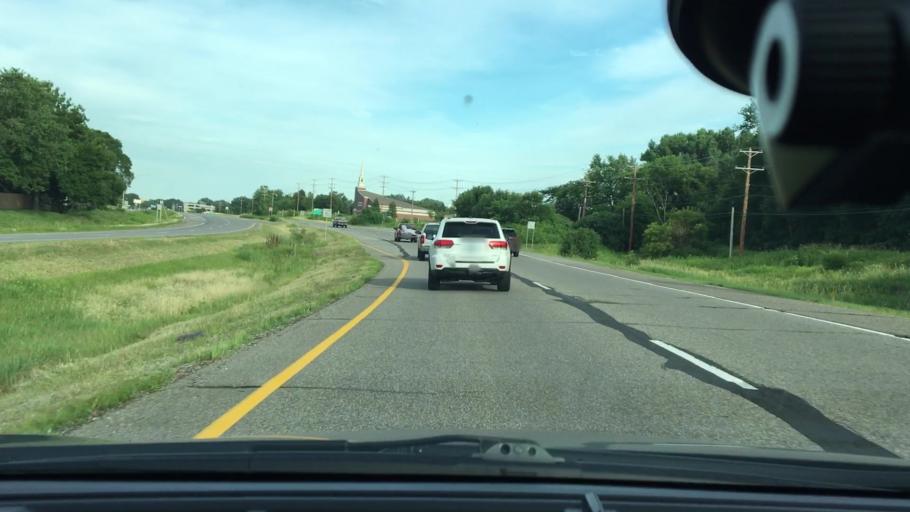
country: US
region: Minnesota
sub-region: Hennepin County
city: Plymouth
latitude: 44.9909
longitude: -93.4321
